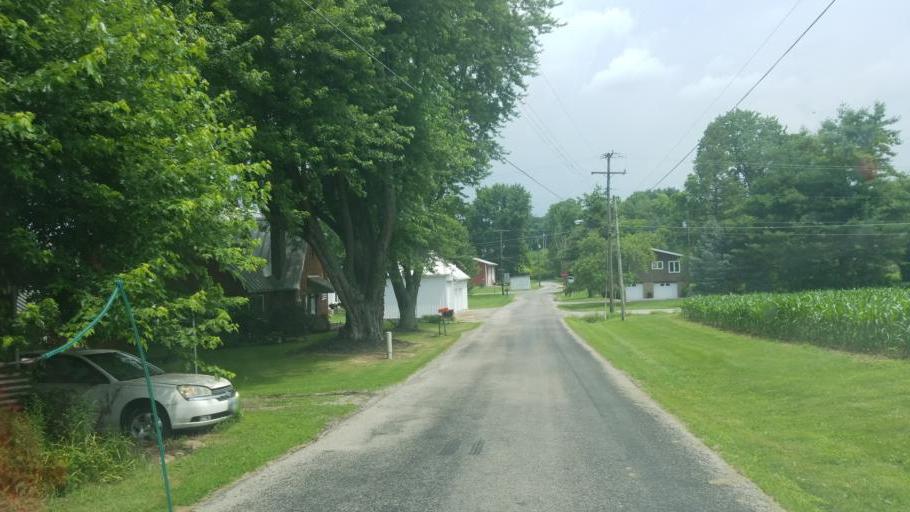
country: US
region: Ohio
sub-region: Wayne County
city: West Salem
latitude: 40.8391
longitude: -82.1026
